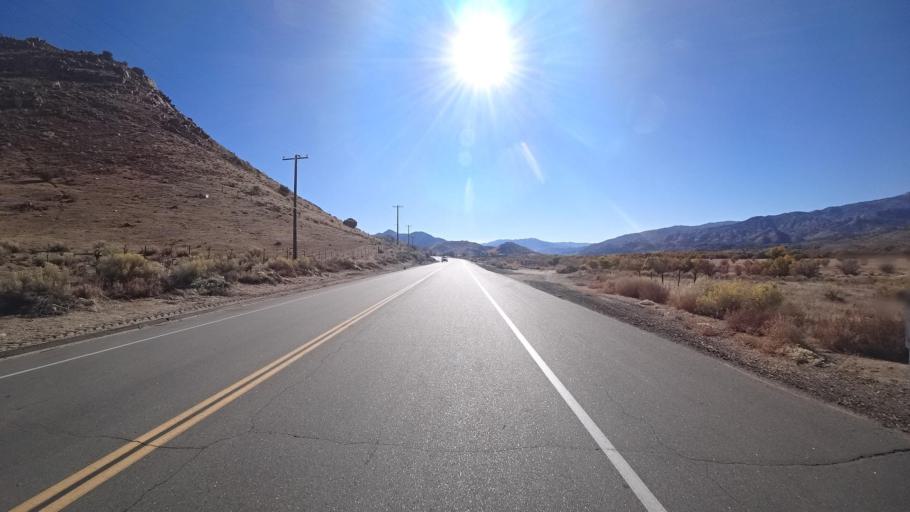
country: US
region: California
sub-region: Kern County
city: Kernville
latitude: 35.7192
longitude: -118.4175
